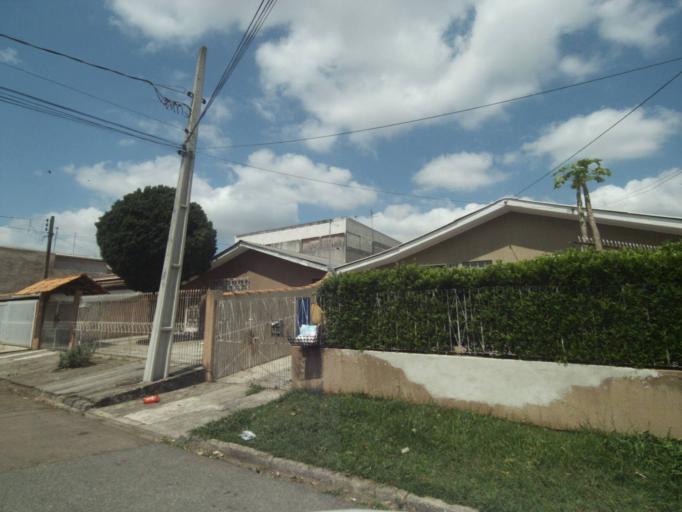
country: BR
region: Parana
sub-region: Sao Jose Dos Pinhais
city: Sao Jose dos Pinhais
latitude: -25.5302
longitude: -49.2617
